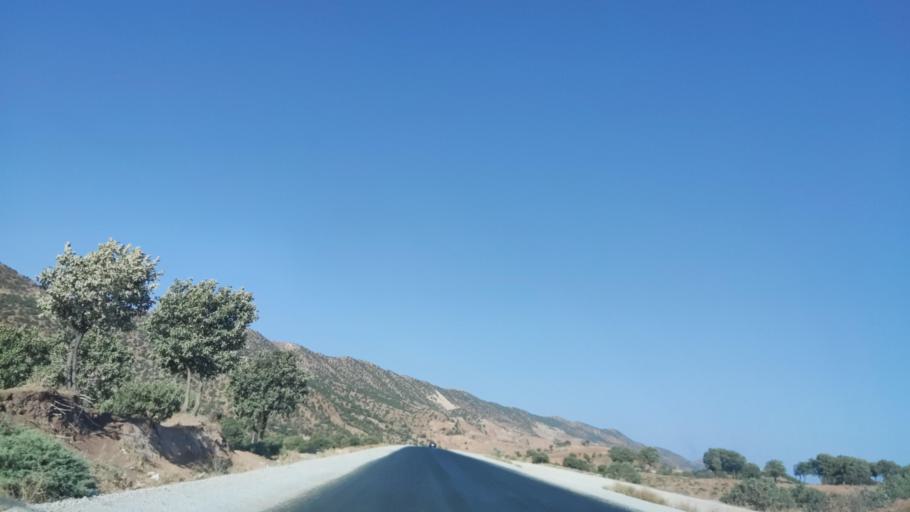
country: IQ
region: Arbil
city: Shaqlawah
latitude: 36.4300
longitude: 44.3278
